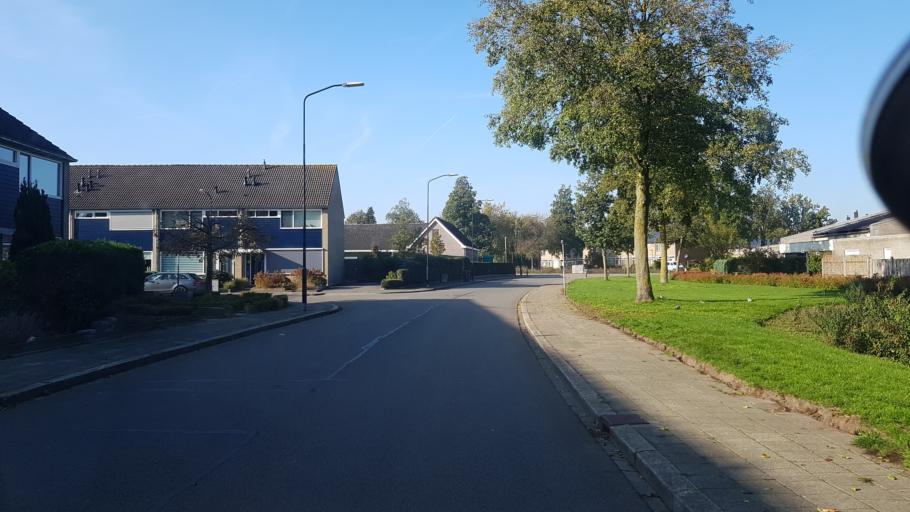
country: NL
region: Gelderland
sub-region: Gemeente Apeldoorn
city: Apeldoorn
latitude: 52.2249
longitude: 5.9807
